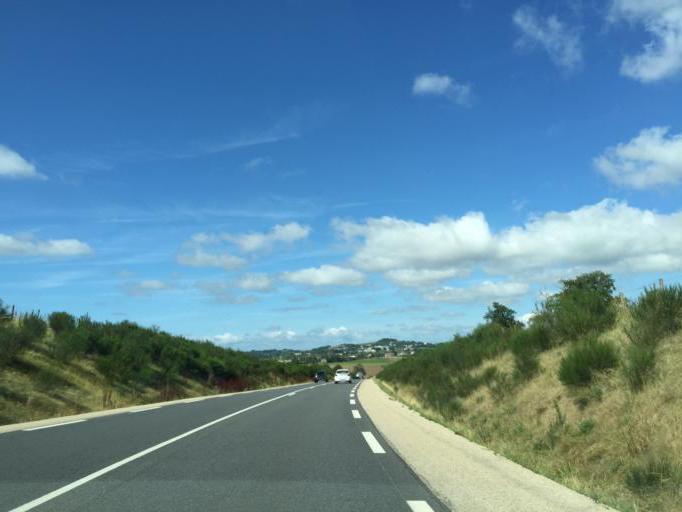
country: FR
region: Midi-Pyrenees
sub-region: Departement de l'Aveyron
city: Rieupeyroux
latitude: 44.3089
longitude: 2.2916
